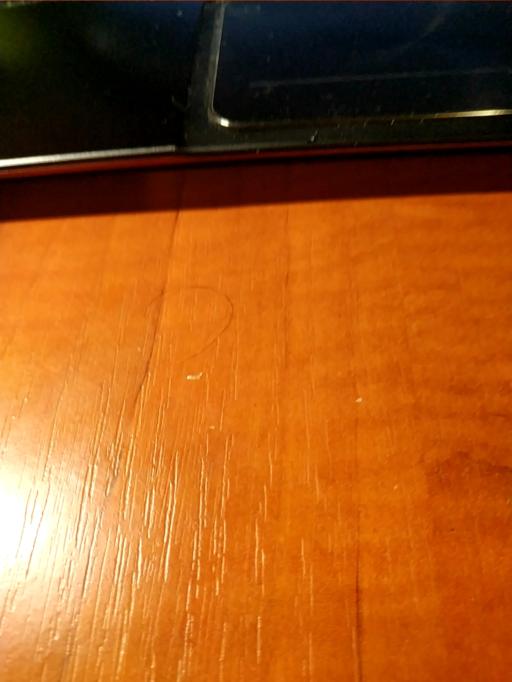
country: RU
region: Kaluga
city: Iznoski
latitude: 54.8579
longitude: 35.3382
